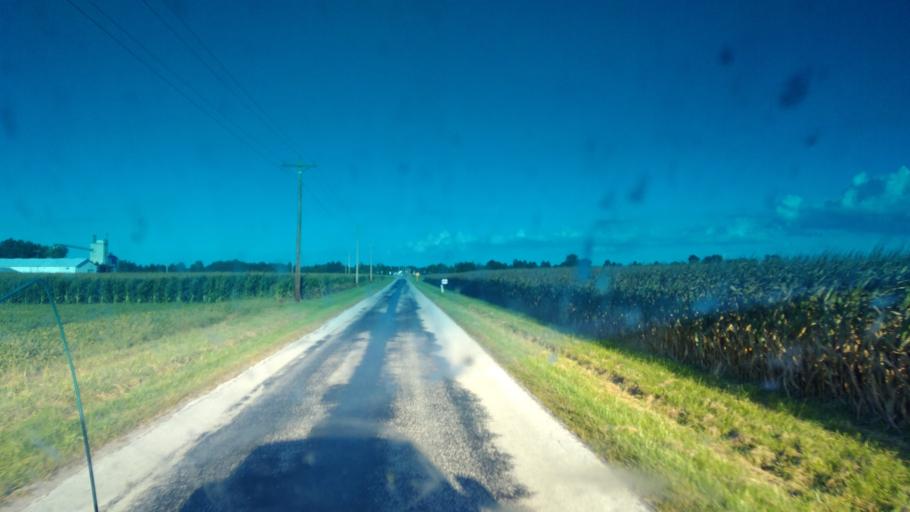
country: US
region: Ohio
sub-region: Wyandot County
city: Carey
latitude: 40.9015
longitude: -83.3507
